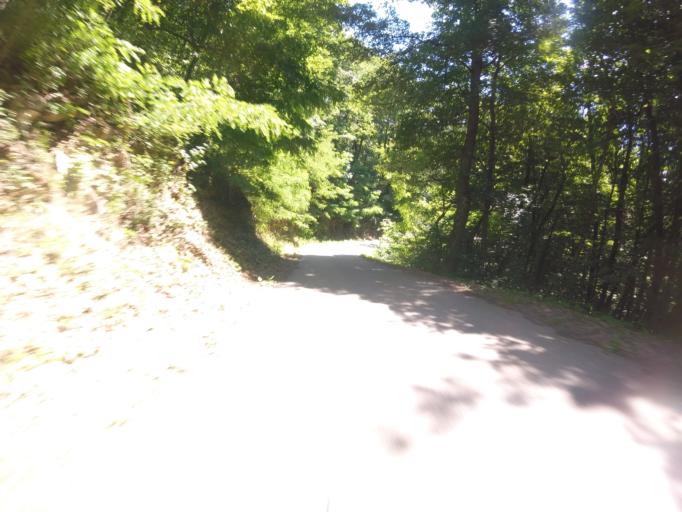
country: HR
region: Karlovacka
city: Ozalj
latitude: 45.6880
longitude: 15.4109
